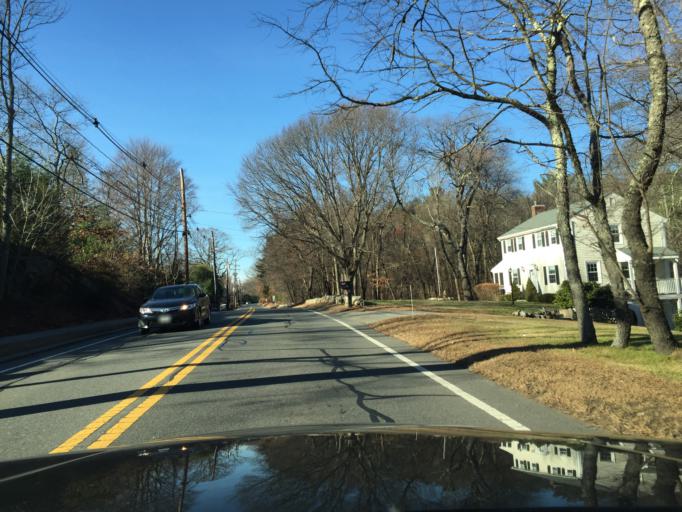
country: US
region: Massachusetts
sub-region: Middlesex County
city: Arlington
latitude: 42.4343
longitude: -71.1863
